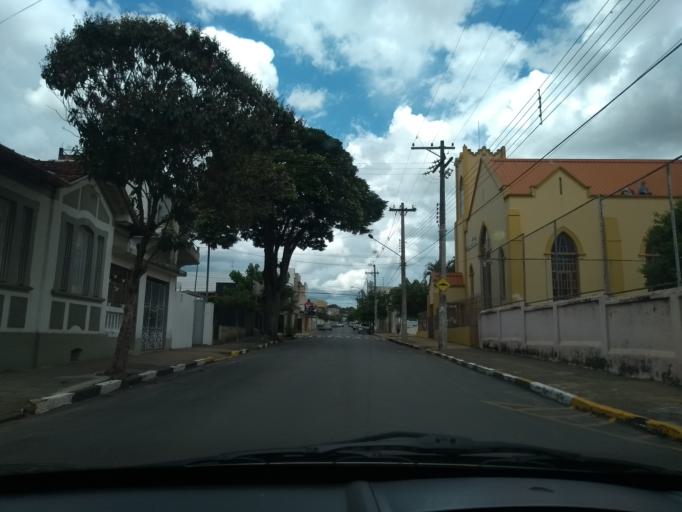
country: BR
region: Sao Paulo
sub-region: Casa Branca
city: Casa Branca
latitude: -21.7755
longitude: -47.0834
